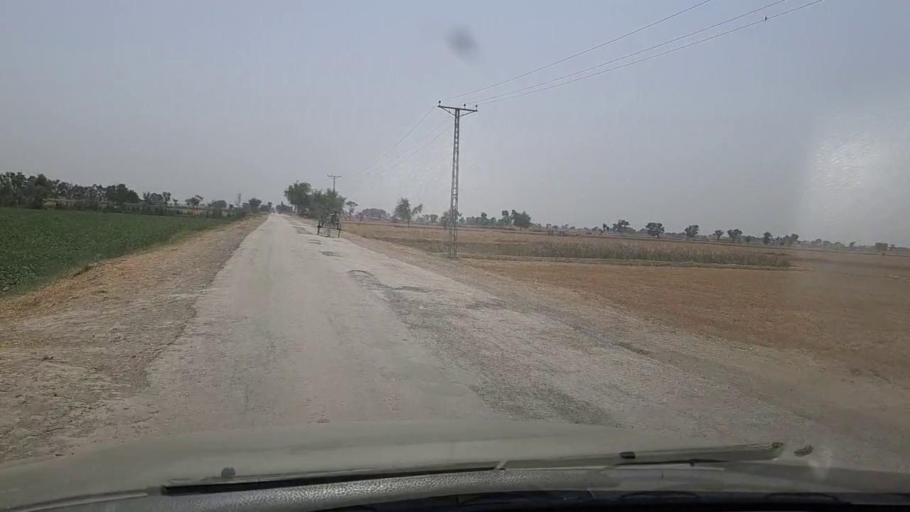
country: PK
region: Sindh
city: Miro Khan
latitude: 27.7145
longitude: 68.0664
